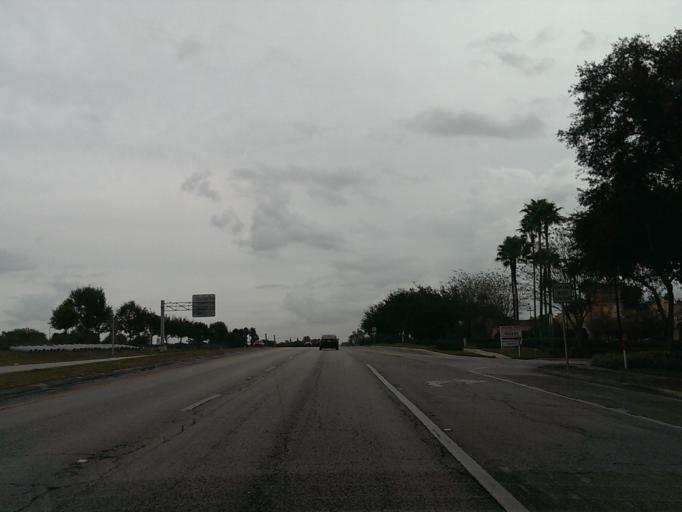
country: US
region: Florida
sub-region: Orange County
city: Gotha
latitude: 28.5518
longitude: -81.5178
